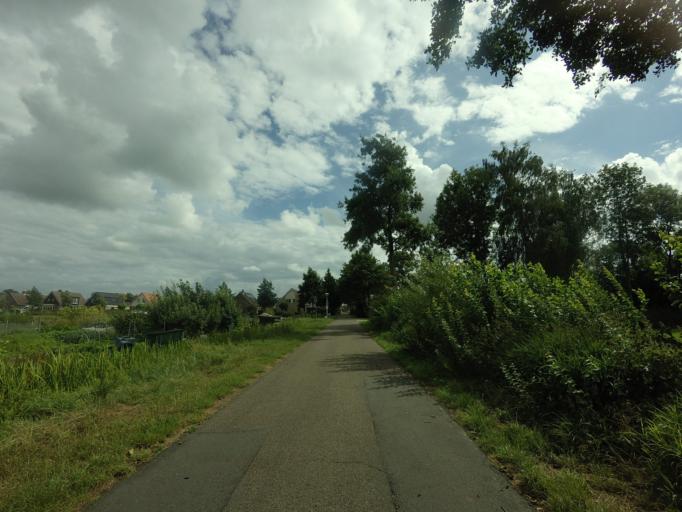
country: NL
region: Overijssel
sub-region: Gemeente Steenwijkerland
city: Wanneperveen
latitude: 52.7073
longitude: 6.1203
